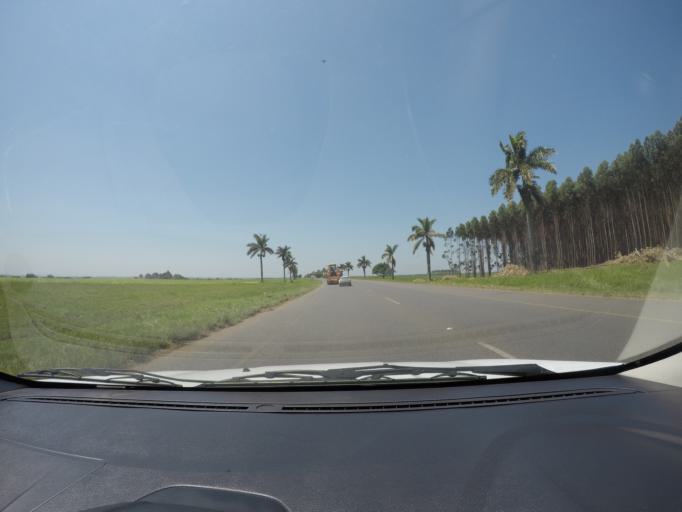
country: ZA
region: KwaZulu-Natal
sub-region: uThungulu District Municipality
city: eSikhawini
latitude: -28.8151
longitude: 31.9543
